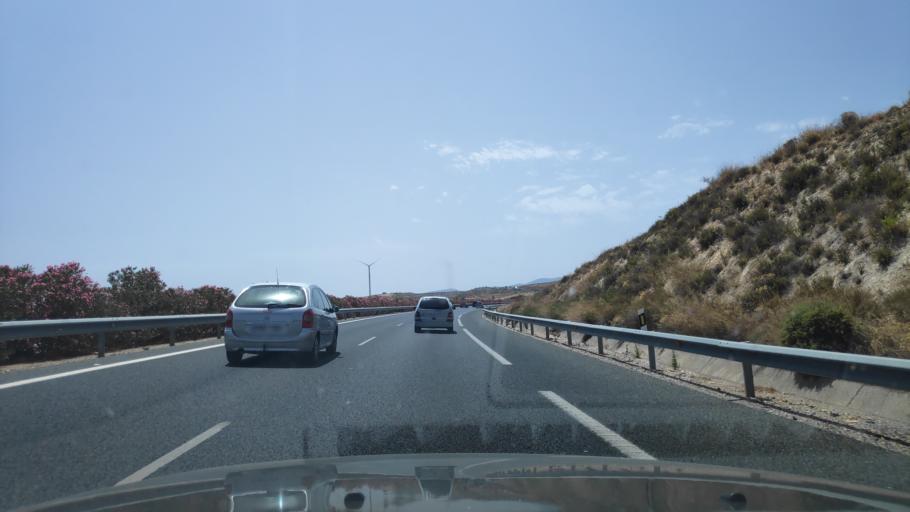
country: ES
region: Andalusia
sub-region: Provincia de Granada
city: Padul
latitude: 37.0188
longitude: -3.6412
